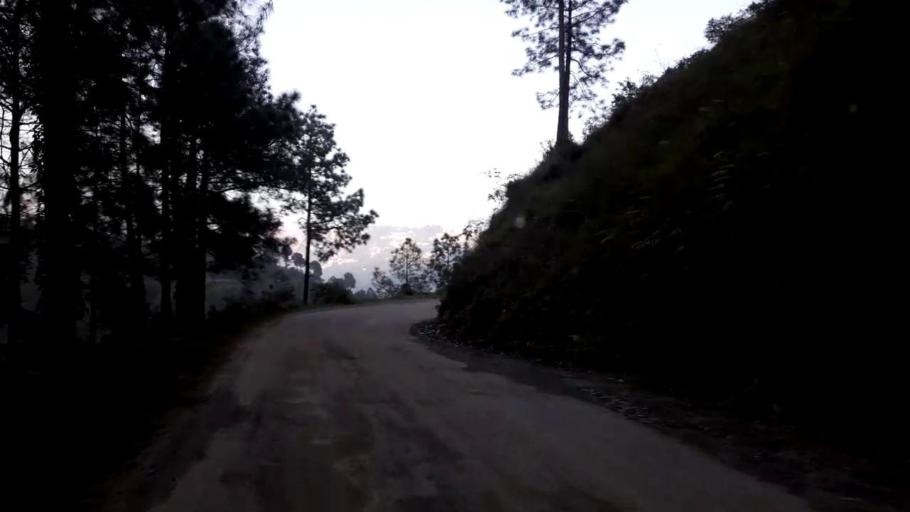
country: IN
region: Himachal Pradesh
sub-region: Shimla
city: Shimla
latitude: 31.0650
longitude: 77.1485
